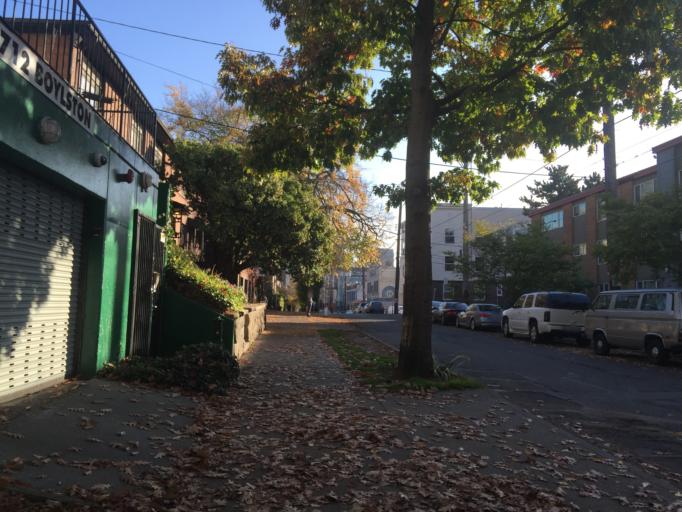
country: US
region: Washington
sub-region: King County
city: Seattle
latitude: 47.6169
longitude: -122.3234
